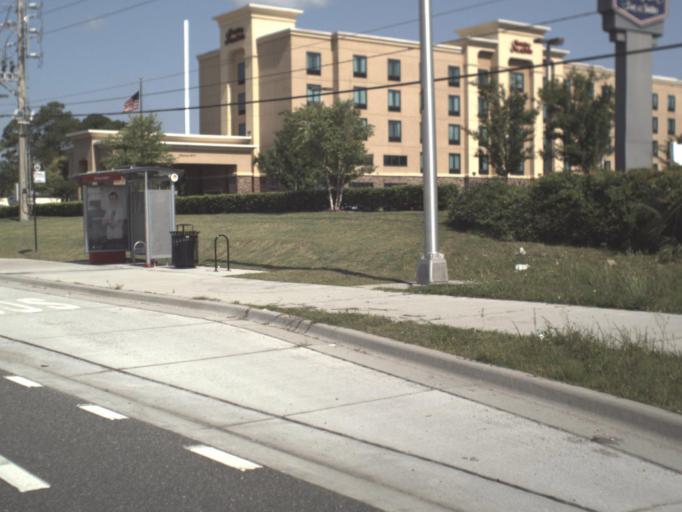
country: US
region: Florida
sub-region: Duval County
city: Jacksonville Beach
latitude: 30.2878
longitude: -81.4560
